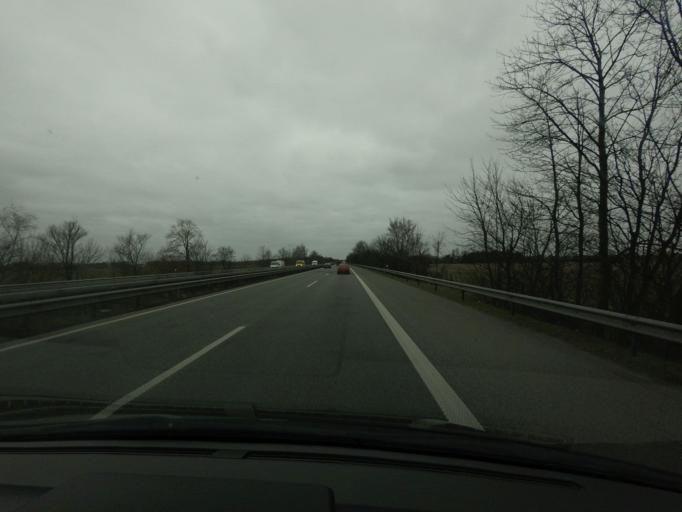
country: DE
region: Lower Saxony
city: Hatten
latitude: 53.0829
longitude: 8.3120
